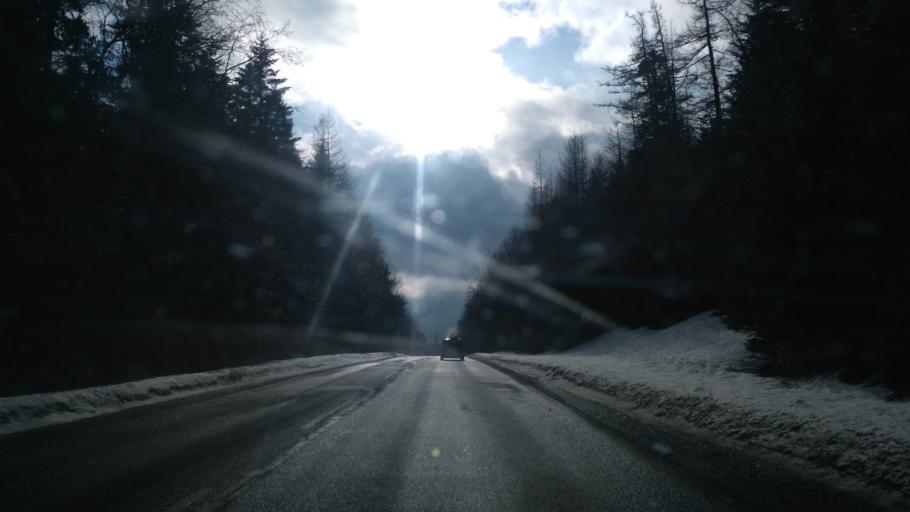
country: SK
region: Presovsky
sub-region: Okres Poprad
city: Nova Lesna
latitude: 49.1922
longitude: 20.2979
